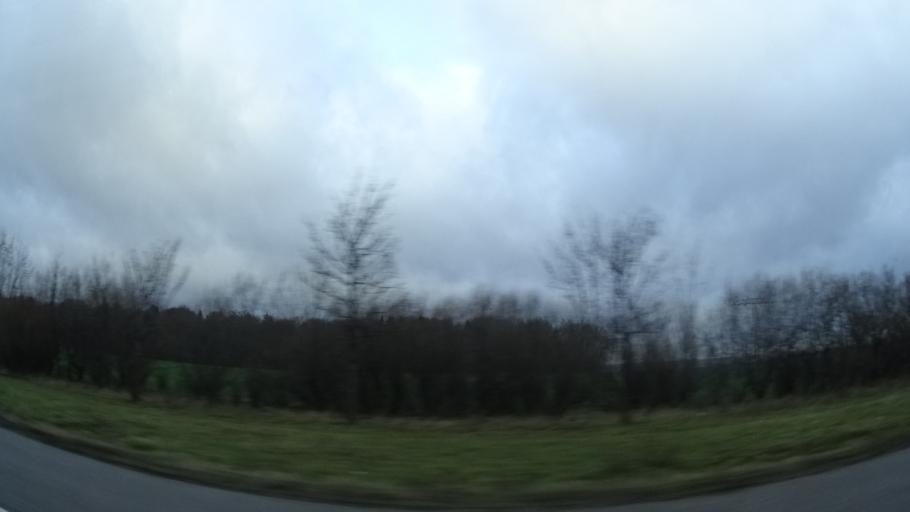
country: DE
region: Thuringia
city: Hetschburg
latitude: 50.9454
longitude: 11.2904
